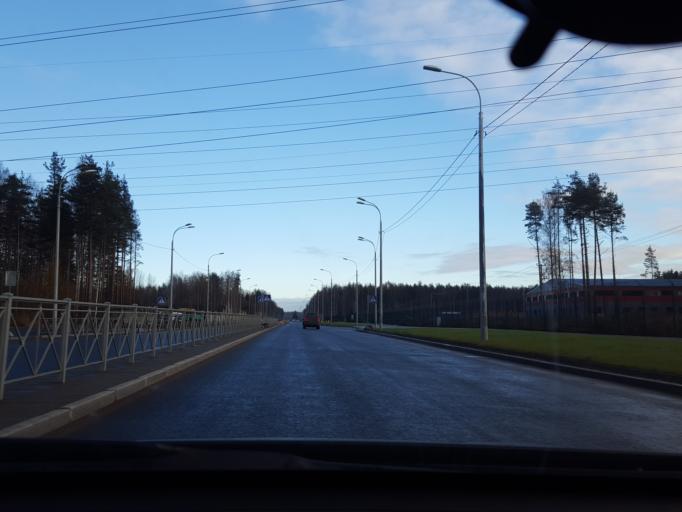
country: RU
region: St.-Petersburg
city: Pargolovo
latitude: 60.0555
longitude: 30.2349
